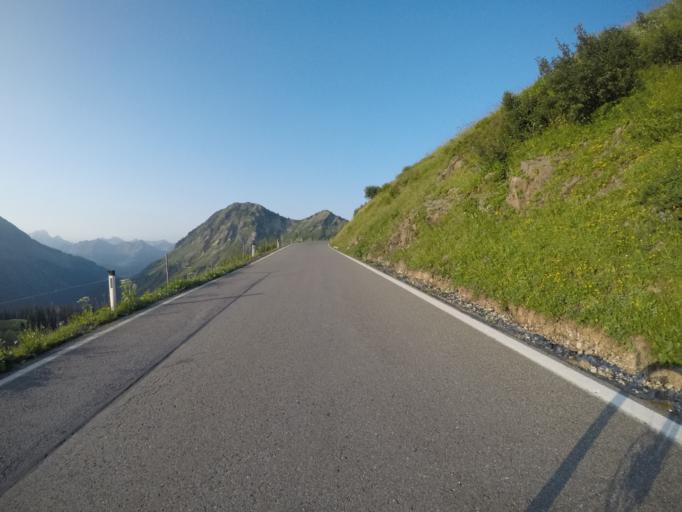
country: AT
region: Vorarlberg
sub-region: Politischer Bezirk Bludenz
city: Blons
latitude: 47.2771
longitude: 9.8372
